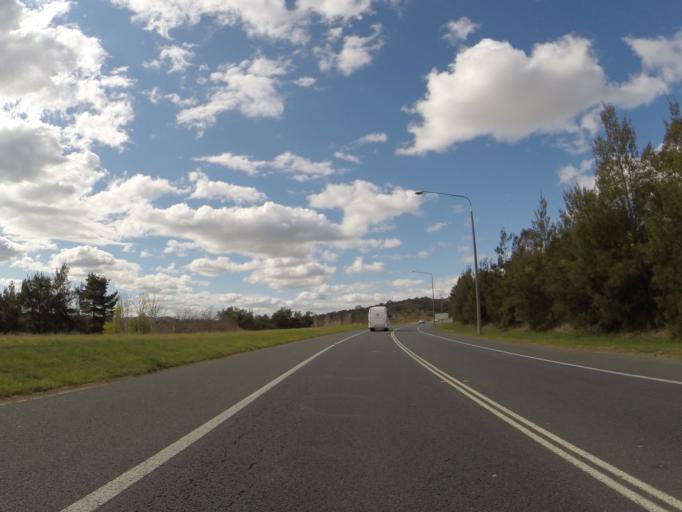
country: AU
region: Australian Capital Territory
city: Belconnen
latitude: -35.2041
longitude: 149.0901
